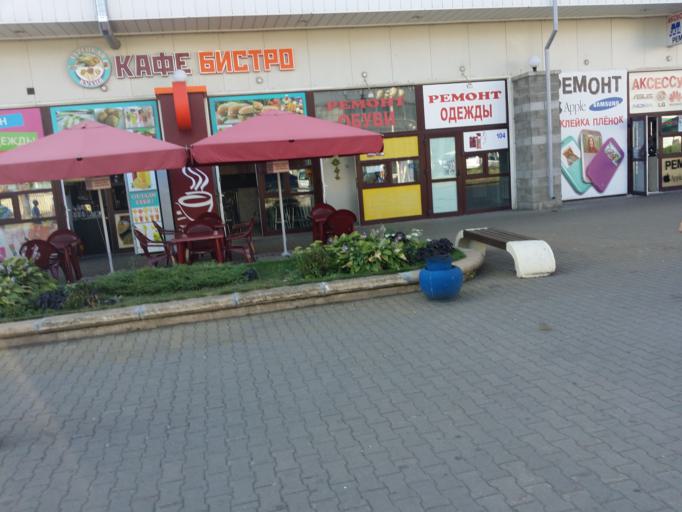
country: BY
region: Minsk
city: Minsk
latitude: 53.9196
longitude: 27.5814
